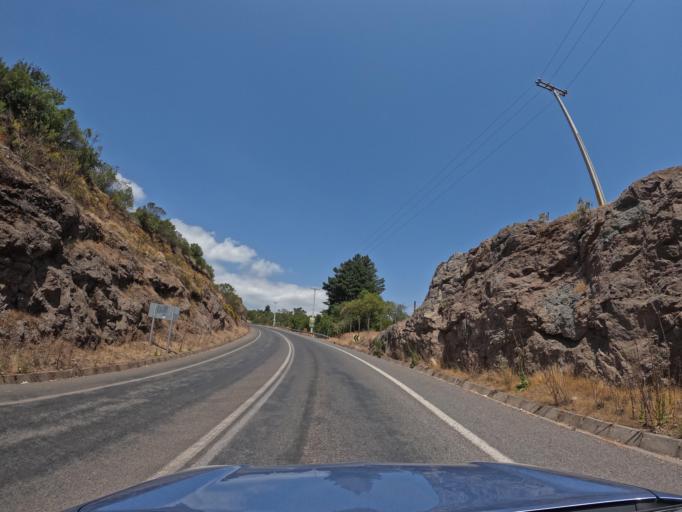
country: CL
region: Maule
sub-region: Provincia de Curico
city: Molina
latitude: -35.1809
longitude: -71.1177
